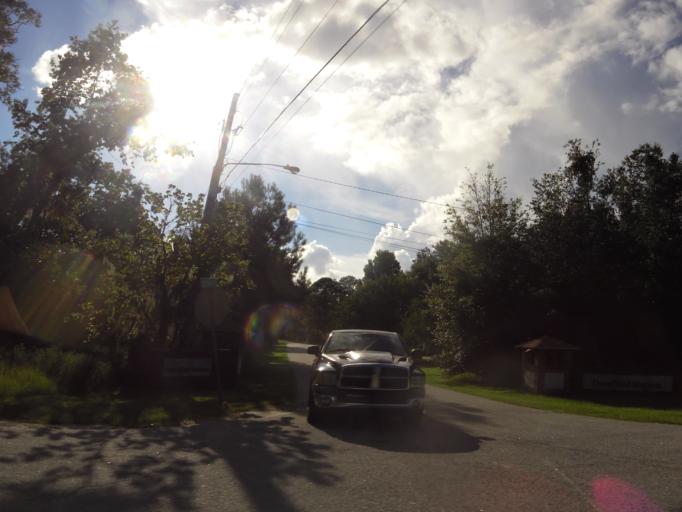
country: US
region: Georgia
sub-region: Glynn County
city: Country Club Estates
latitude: 31.2423
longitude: -81.4506
